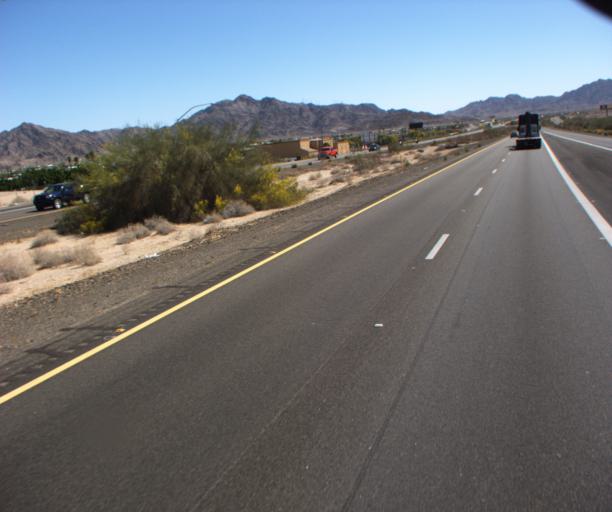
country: US
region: Arizona
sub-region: Yuma County
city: Fortuna Foothills
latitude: 32.6693
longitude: -114.4061
